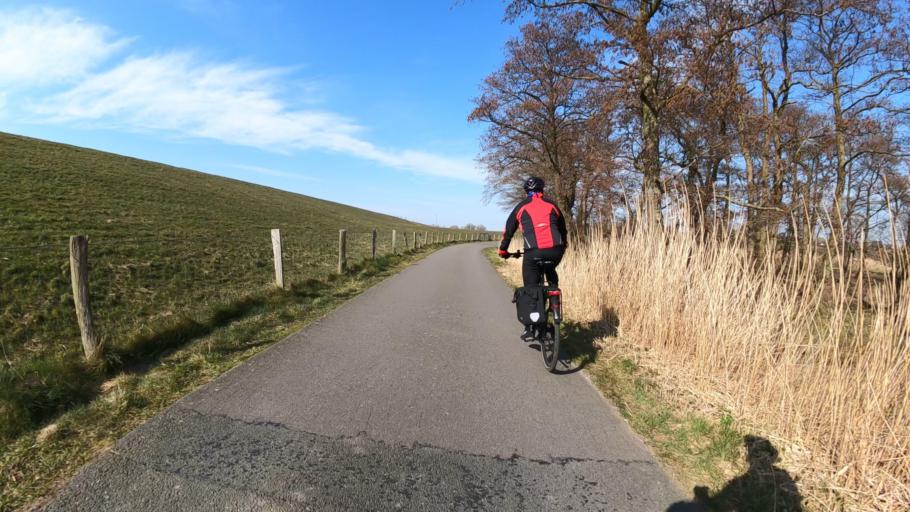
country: DE
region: Schleswig-Holstein
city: Haseldorf
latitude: 53.6432
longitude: 9.5639
